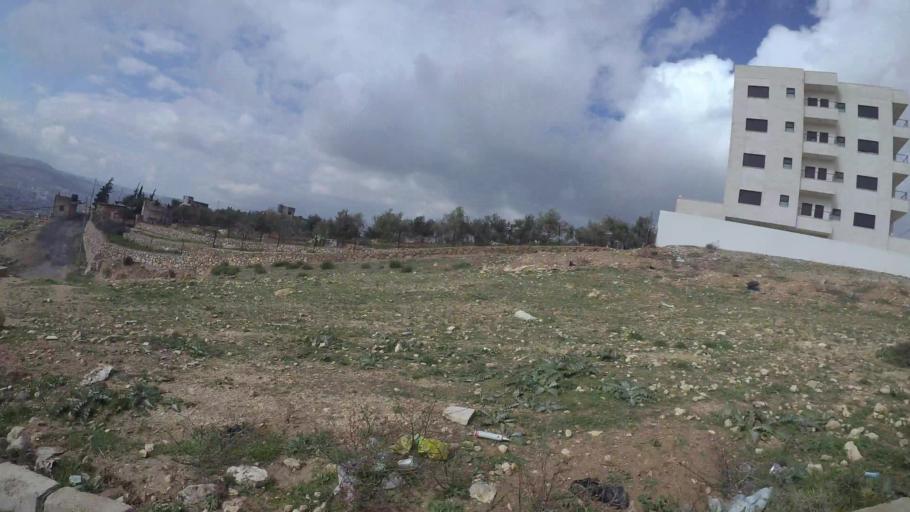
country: JO
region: Amman
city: Al Jubayhah
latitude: 32.0608
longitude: 35.8604
